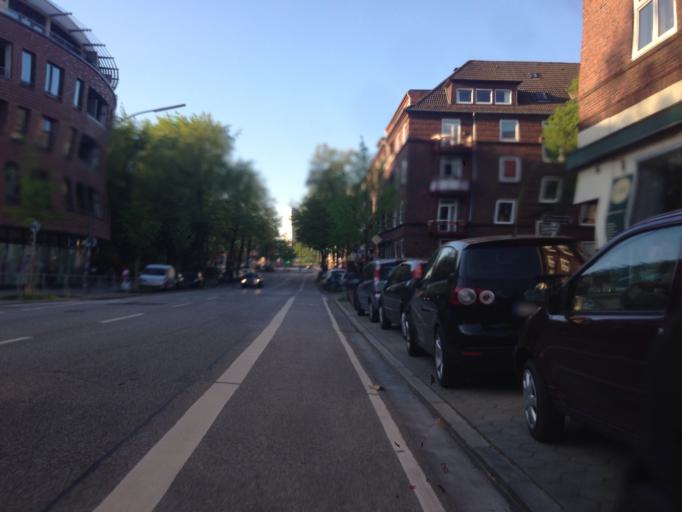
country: DE
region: Hamburg
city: Borgfelde
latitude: 53.5629
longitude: 10.0565
